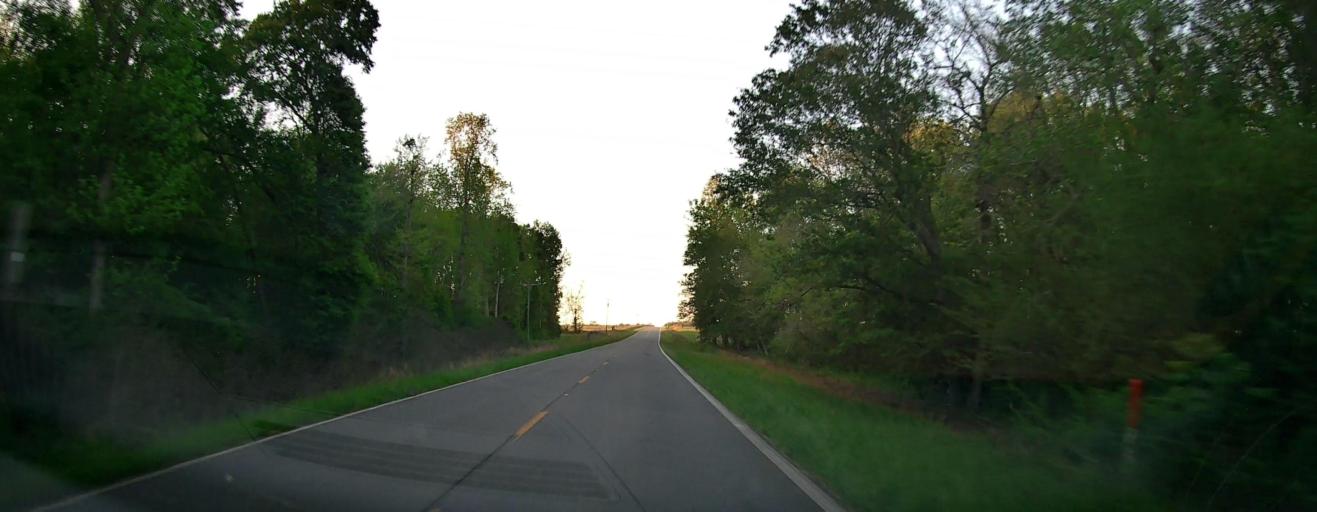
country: US
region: Georgia
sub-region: Ben Hill County
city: Fitzgerald
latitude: 31.7233
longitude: -83.3099
